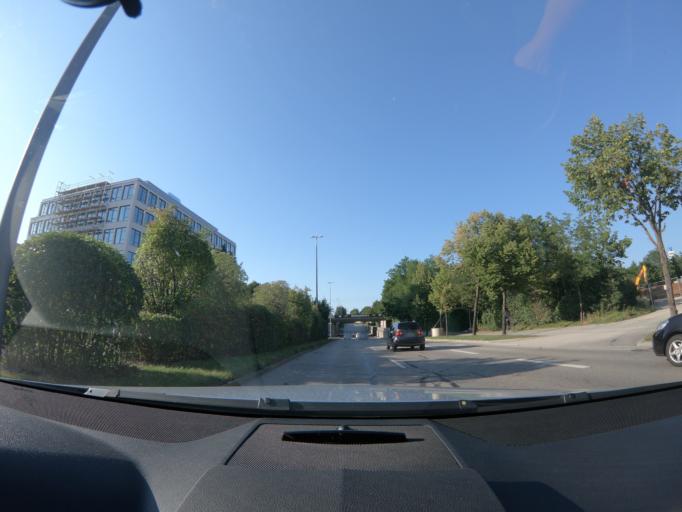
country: DE
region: Bavaria
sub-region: Upper Bavaria
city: Bogenhausen
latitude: 48.1896
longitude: 11.5844
